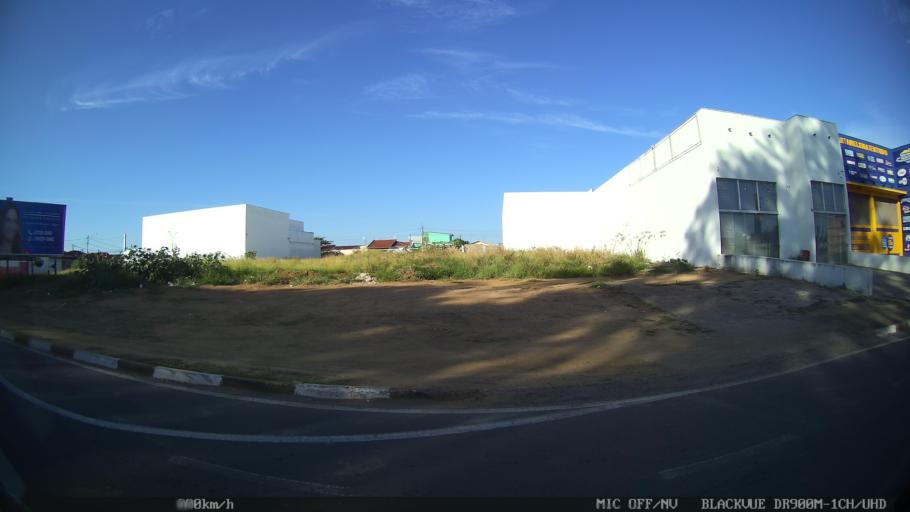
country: BR
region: Sao Paulo
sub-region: Franca
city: Franca
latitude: -20.5204
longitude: -47.3706
